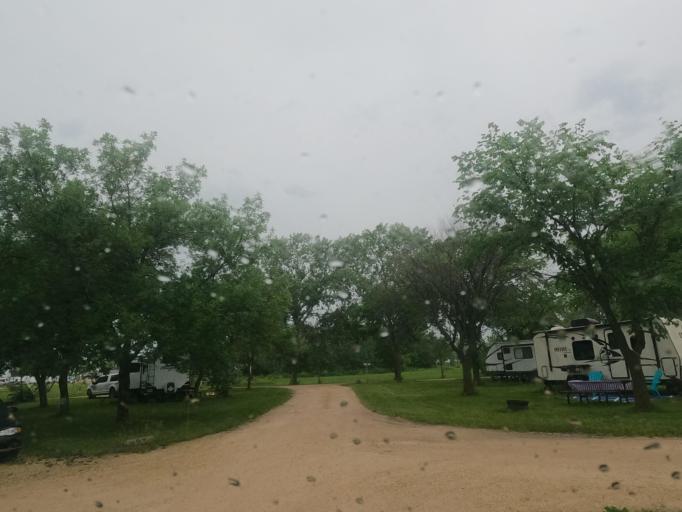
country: CA
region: Manitoba
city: Winnipeg
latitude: 49.8282
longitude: -96.9771
